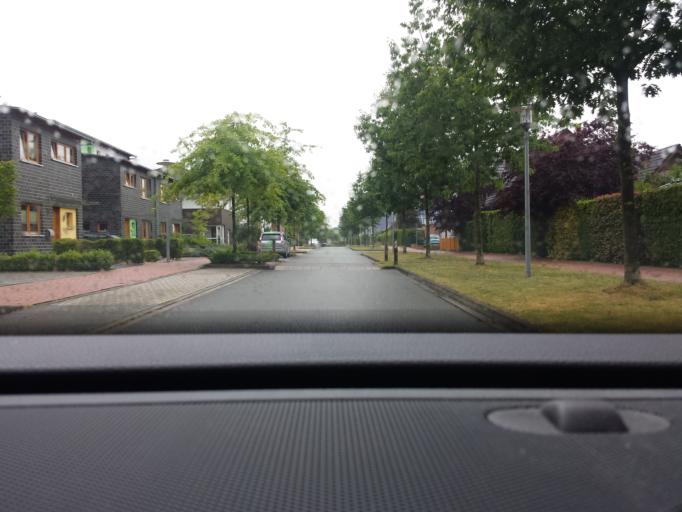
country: DE
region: North Rhine-Westphalia
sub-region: Regierungsbezirk Munster
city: Ahaus
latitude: 52.0733
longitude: 6.9877
